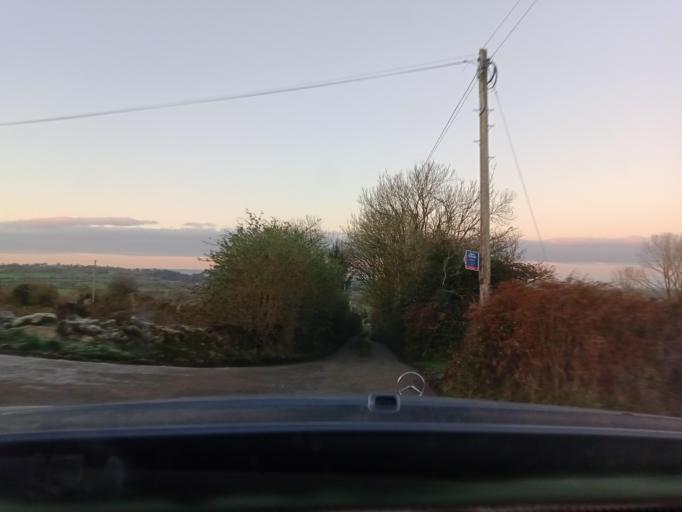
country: IE
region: Leinster
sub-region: Kilkenny
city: Graiguenamanagh
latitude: 52.5829
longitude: -6.9633
